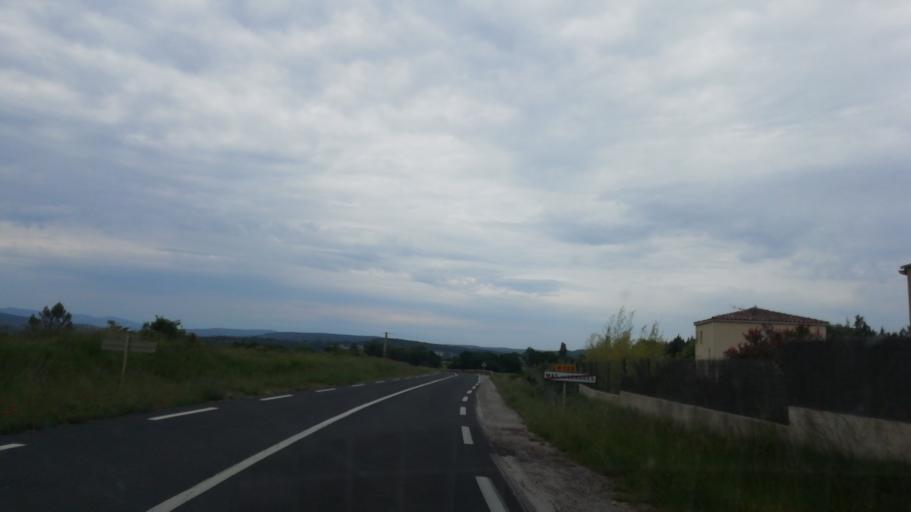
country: FR
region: Languedoc-Roussillon
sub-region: Departement de l'Herault
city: Saint-Martin-de-Londres
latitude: 43.7884
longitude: 3.7591
